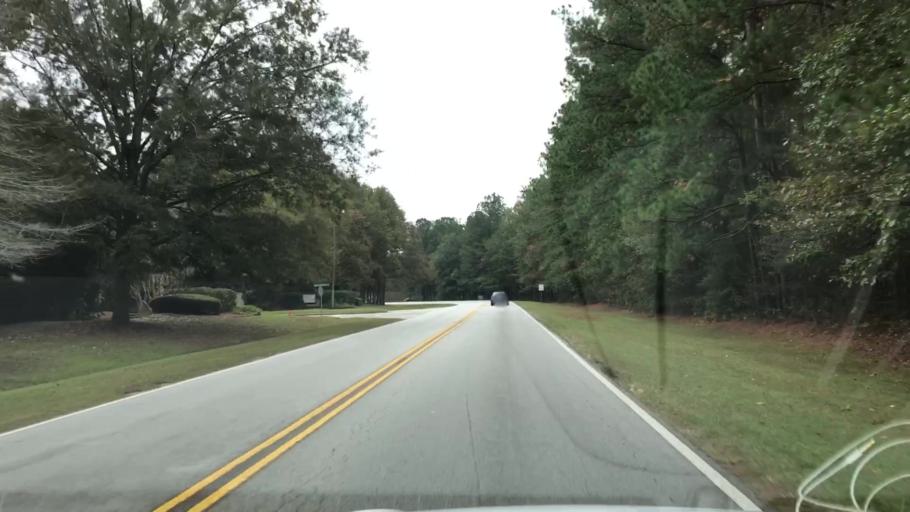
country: US
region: South Carolina
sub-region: Berkeley County
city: Goose Creek
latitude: 33.0101
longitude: -80.0596
